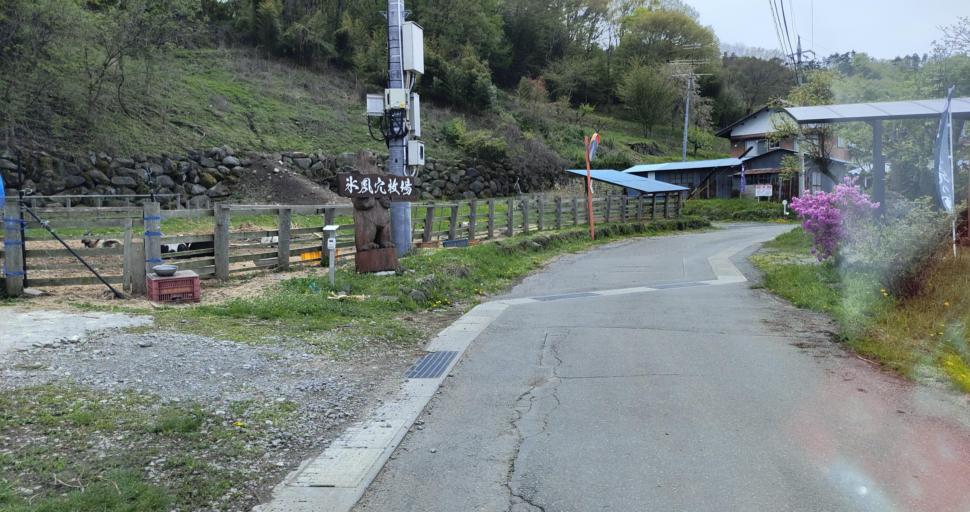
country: JP
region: Nagano
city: Komoro
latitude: 36.3270
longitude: 138.3949
